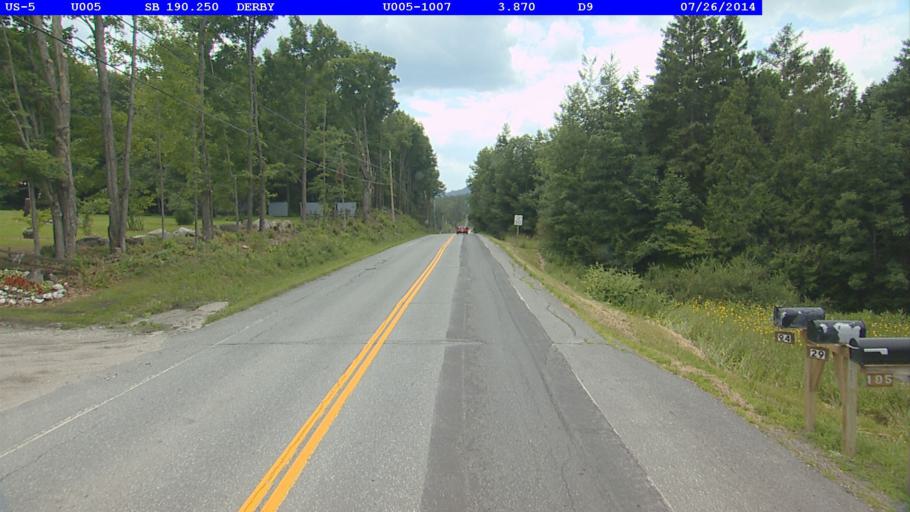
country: US
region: Vermont
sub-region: Orleans County
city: Newport
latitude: 44.9785
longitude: -72.1133
